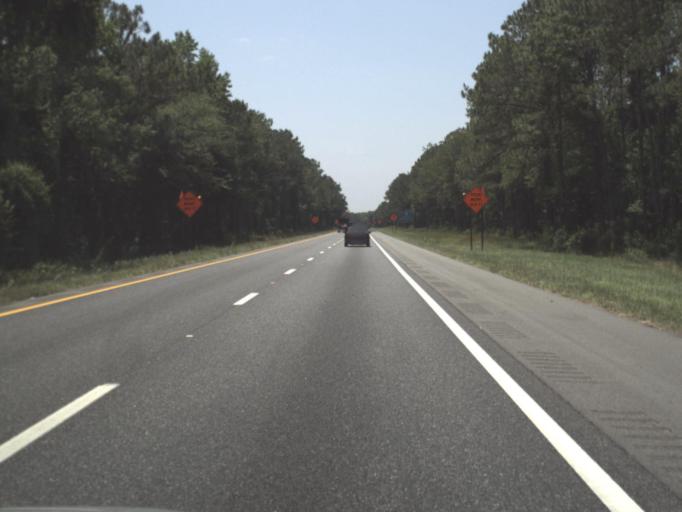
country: US
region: Florida
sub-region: Columbia County
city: Five Points
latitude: 30.2436
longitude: -82.6552
